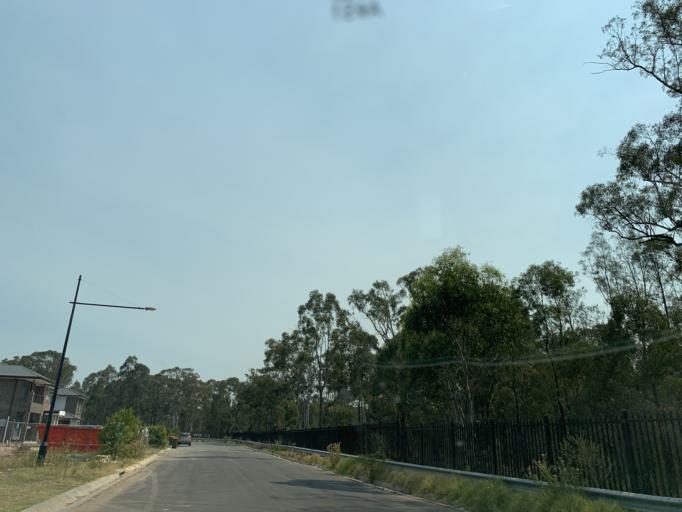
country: AU
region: New South Wales
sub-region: Blacktown
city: Blackett
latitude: -33.7121
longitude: 150.8158
